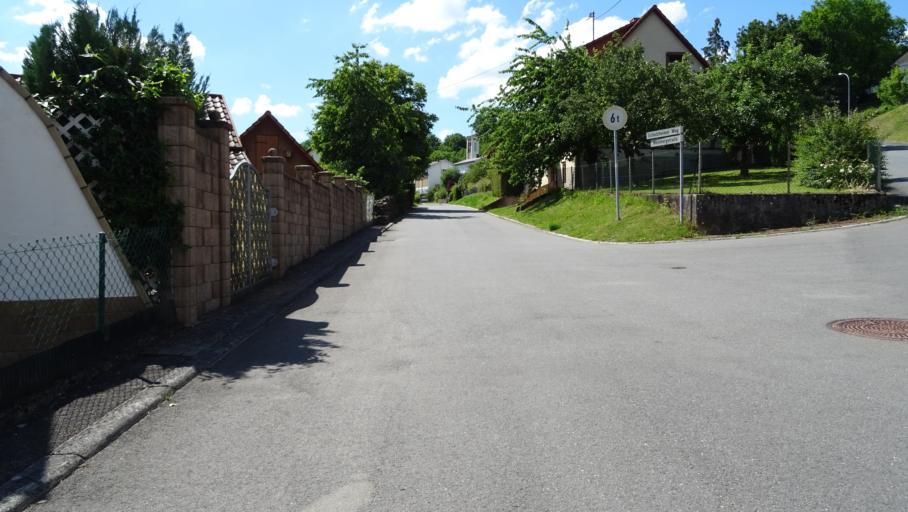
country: DE
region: Baden-Wuerttemberg
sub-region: Karlsruhe Region
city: Adelsheim
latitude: 49.3821
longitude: 9.3791
